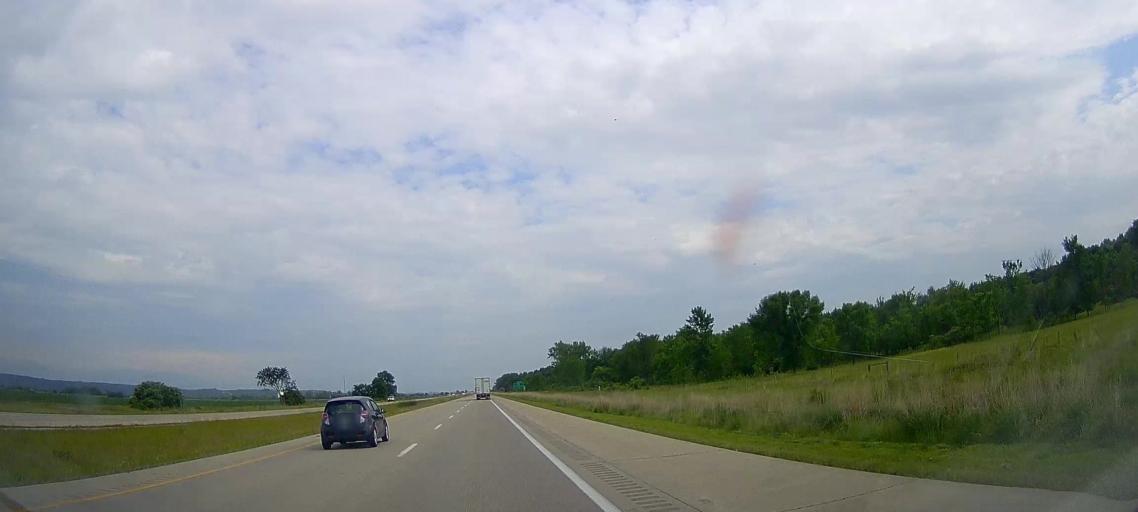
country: US
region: Nebraska
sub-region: Burt County
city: Tekamah
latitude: 41.8185
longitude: -96.0706
